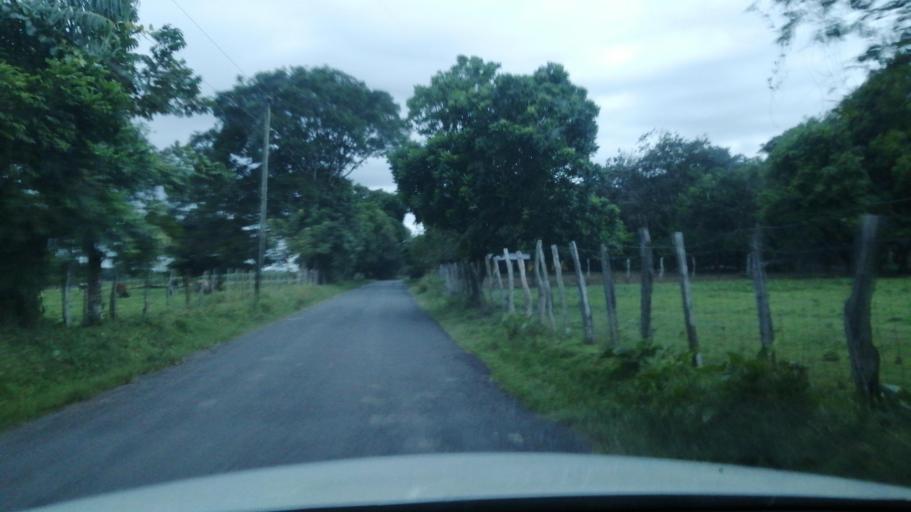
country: PA
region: Chiriqui
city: Alanje
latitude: 8.4024
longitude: -82.4992
